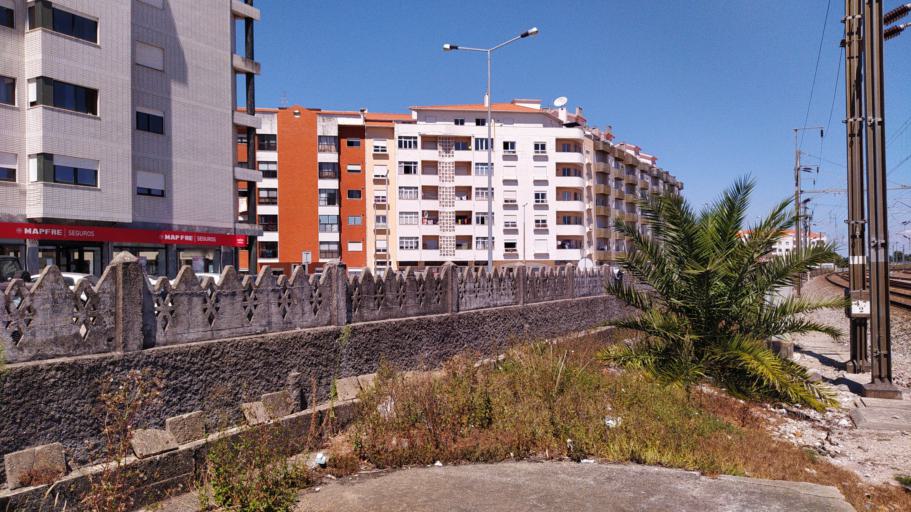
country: PT
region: Aveiro
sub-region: Aveiro
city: Aveiro
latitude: 40.6454
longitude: -8.6399
